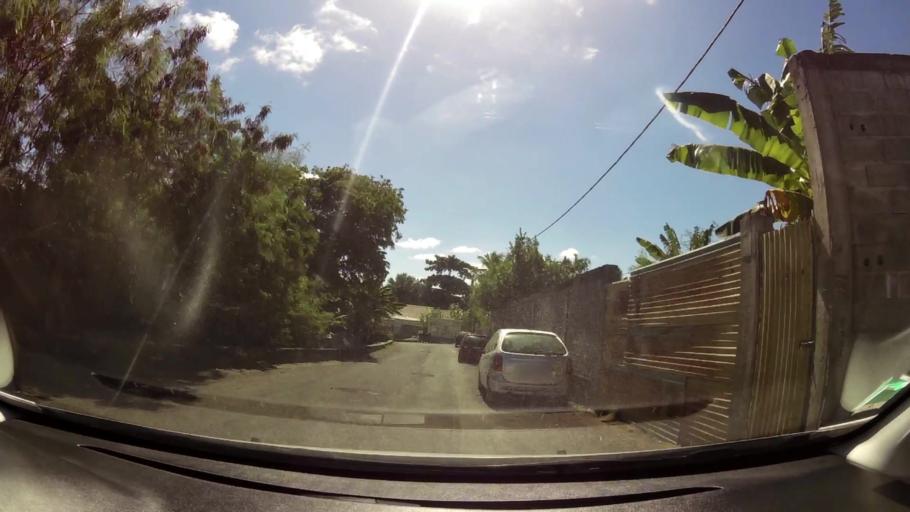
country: YT
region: Pamandzi
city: Pamandzi
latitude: -12.7888
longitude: 45.2809
